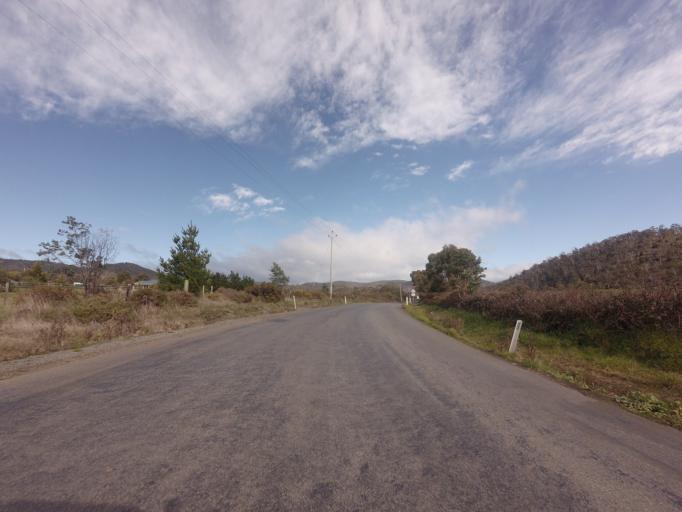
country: AU
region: Tasmania
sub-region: Derwent Valley
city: New Norfolk
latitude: -42.7780
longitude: 147.0198
